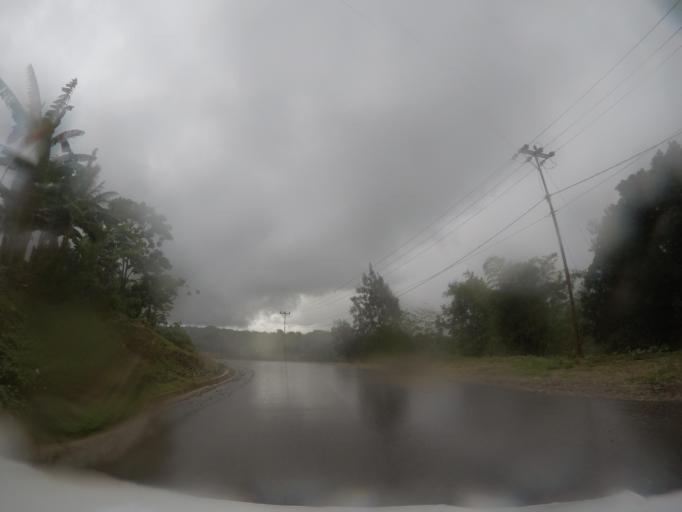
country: TL
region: Baucau
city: Venilale
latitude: -8.6382
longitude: 126.3773
